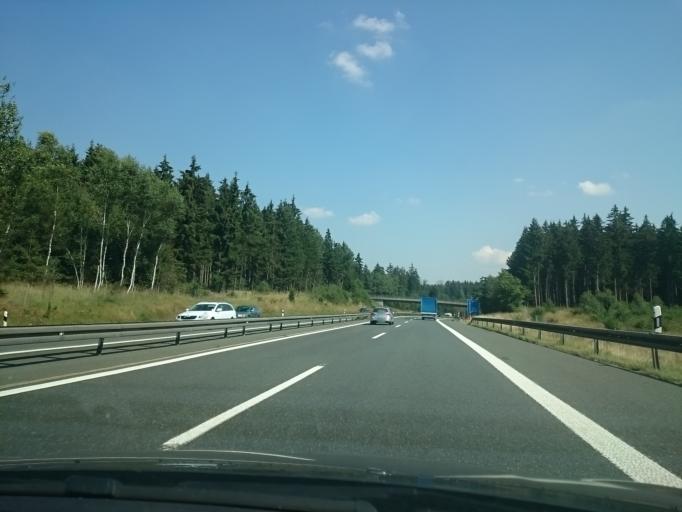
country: DE
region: Bavaria
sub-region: Upper Franconia
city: Koditz
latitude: 50.3381
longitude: 11.8176
